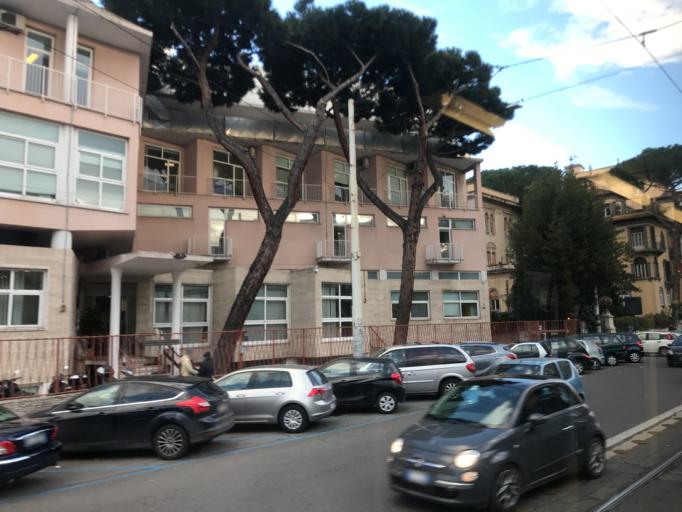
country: IT
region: Latium
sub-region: Citta metropolitana di Roma Capitale
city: Rome
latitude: 41.9107
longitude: 12.5095
